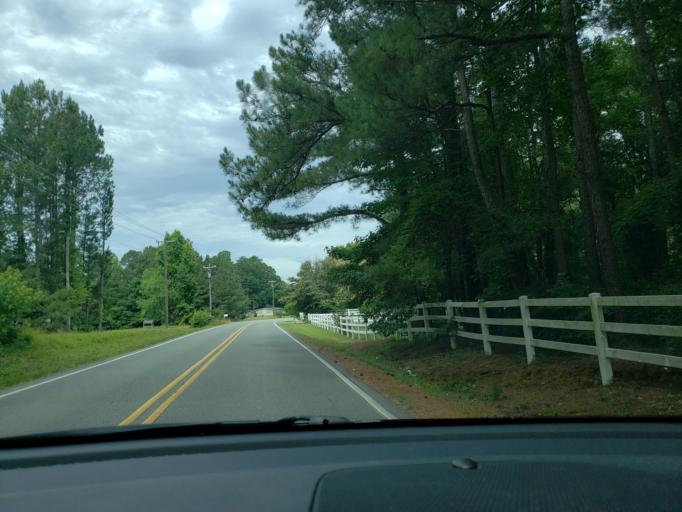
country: US
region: North Carolina
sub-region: Wake County
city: Green Level
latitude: 35.7905
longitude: -78.9670
